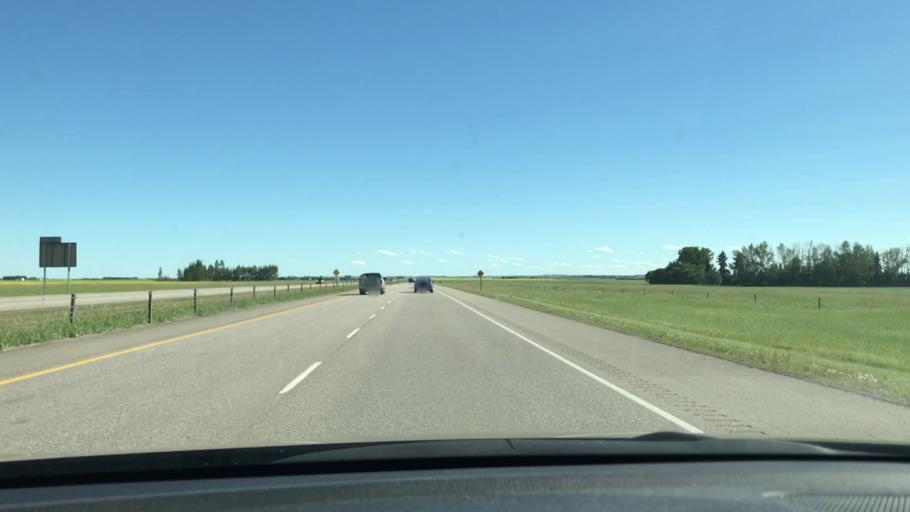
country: CA
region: Alberta
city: Didsbury
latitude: 51.6542
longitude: -114.0256
